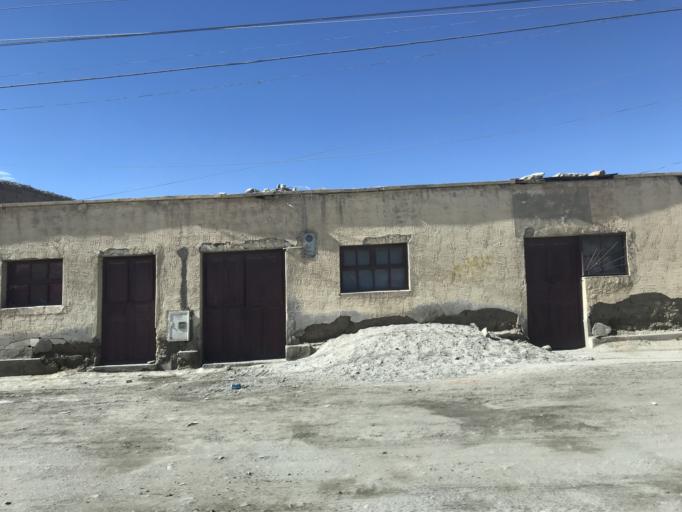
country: BO
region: Potosi
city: Uyuni
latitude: -20.4674
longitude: -66.8252
